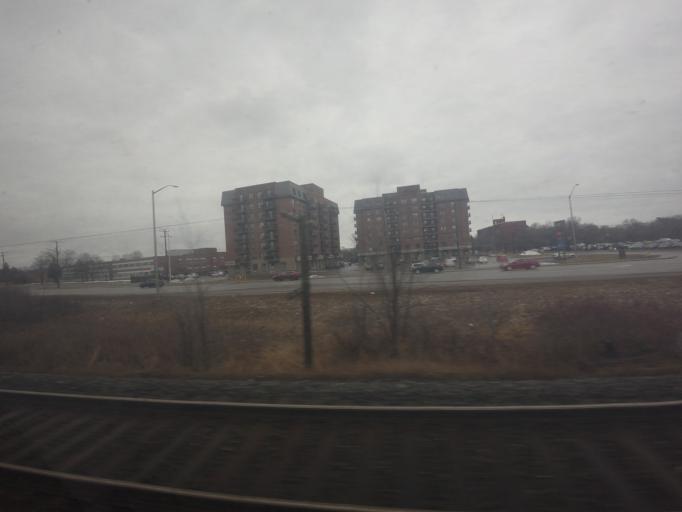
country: CA
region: Ontario
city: Kingston
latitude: 44.2379
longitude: -76.5795
